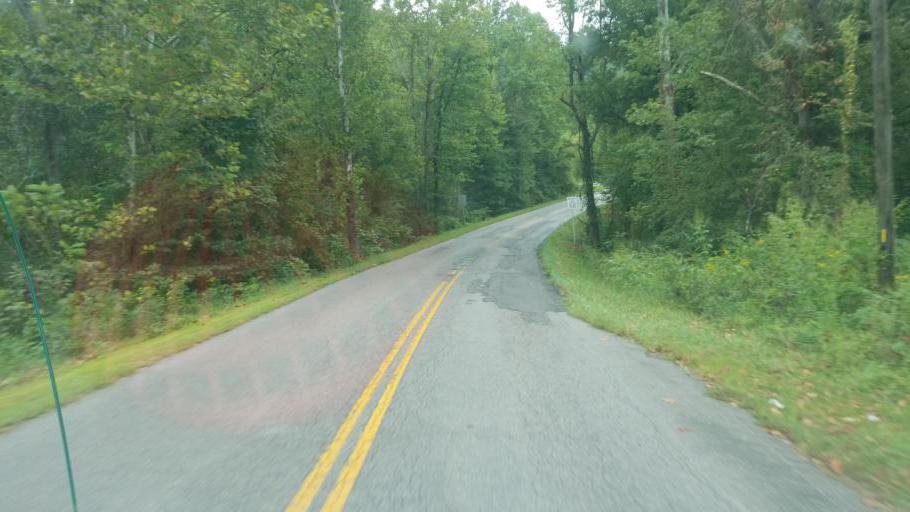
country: US
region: Kentucky
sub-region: Fleming County
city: Flemingsburg
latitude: 38.3704
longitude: -83.5349
